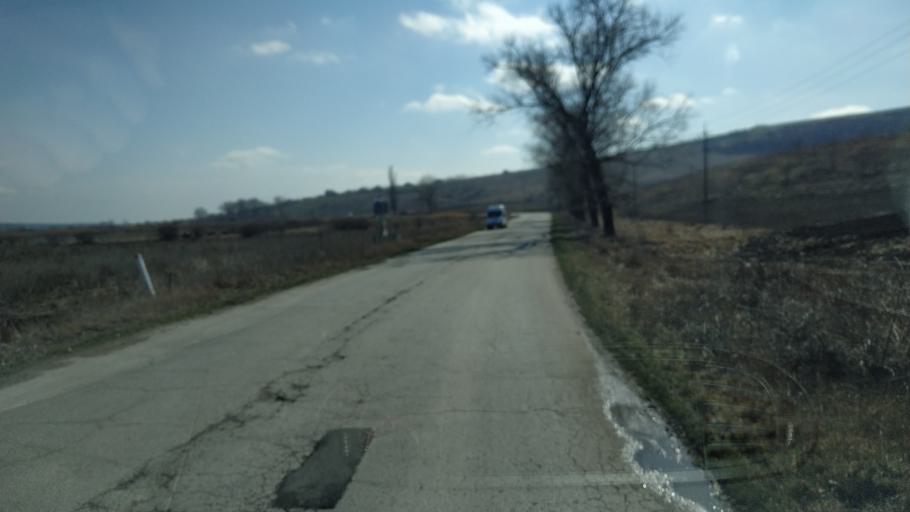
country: MD
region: Hincesti
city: Hincesti
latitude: 46.9437
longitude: 28.6242
